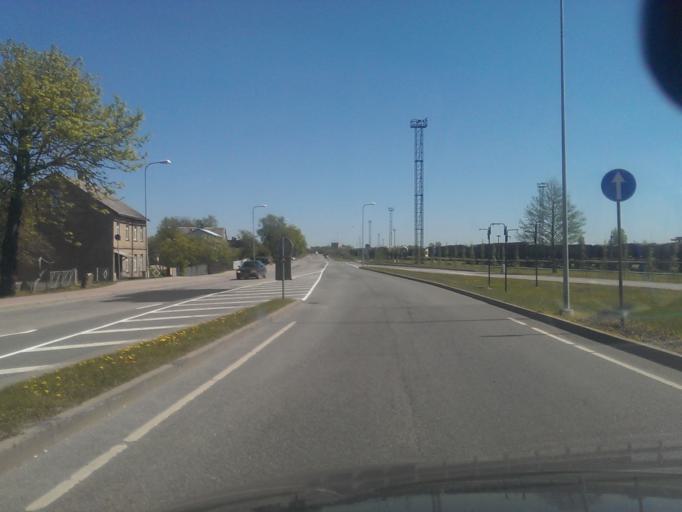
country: LV
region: Ventspils
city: Ventspils
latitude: 57.3963
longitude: 21.5957
